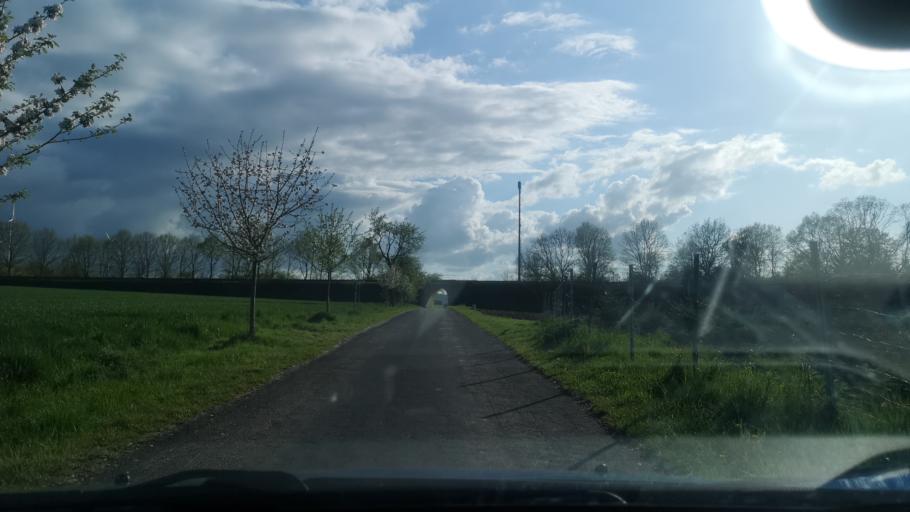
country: DE
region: Lower Saxony
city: Uslar
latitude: 51.6515
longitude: 9.6766
